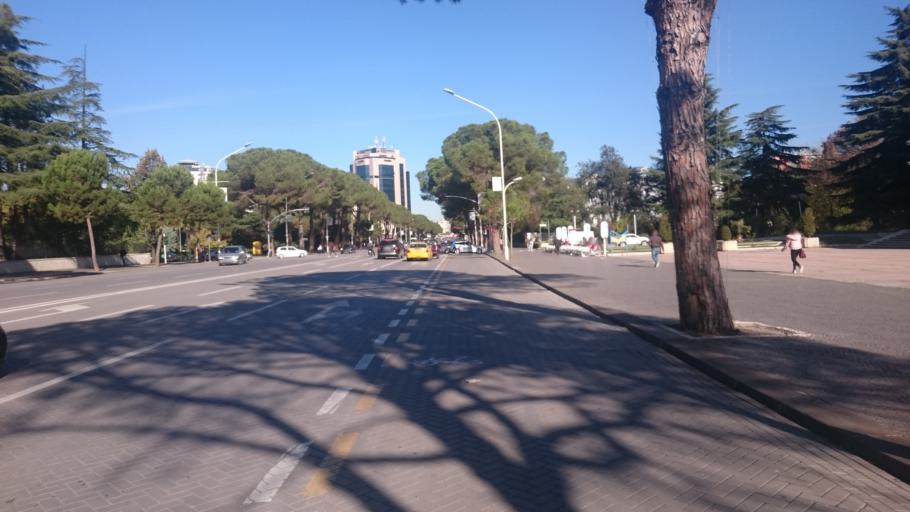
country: AL
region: Tirane
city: Tirana
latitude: 41.3189
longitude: 19.8211
